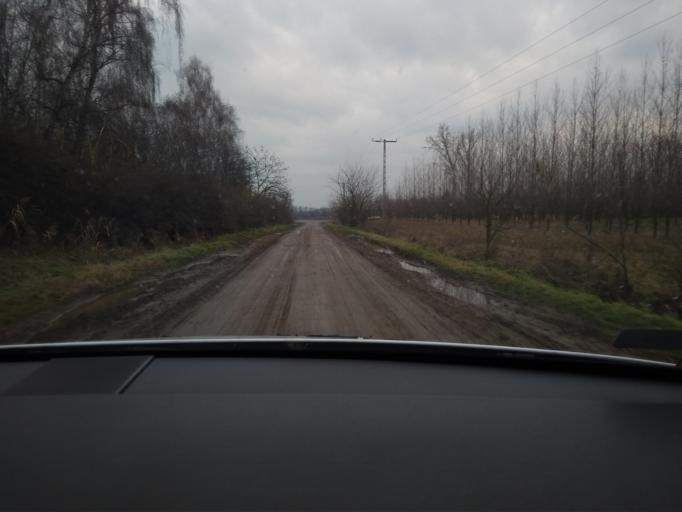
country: HU
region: Szabolcs-Szatmar-Bereg
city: Nyirtelek
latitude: 47.9873
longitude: 21.6665
